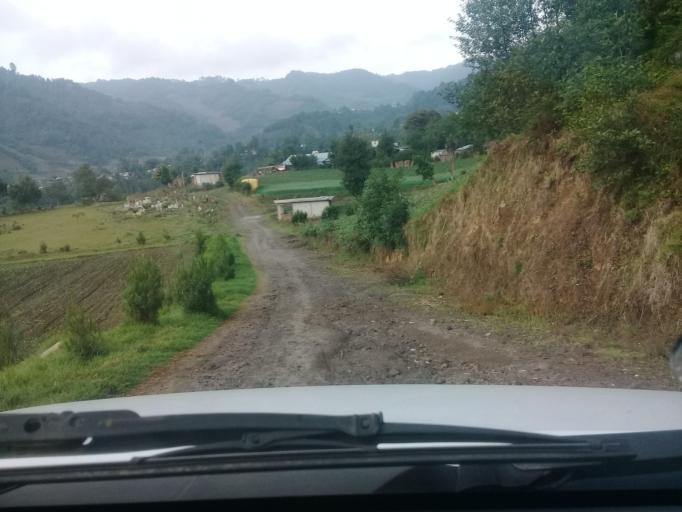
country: MX
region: Veracruz
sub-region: Mariano Escobedo
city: San Isidro el Berro
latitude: 18.9516
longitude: -97.1986
